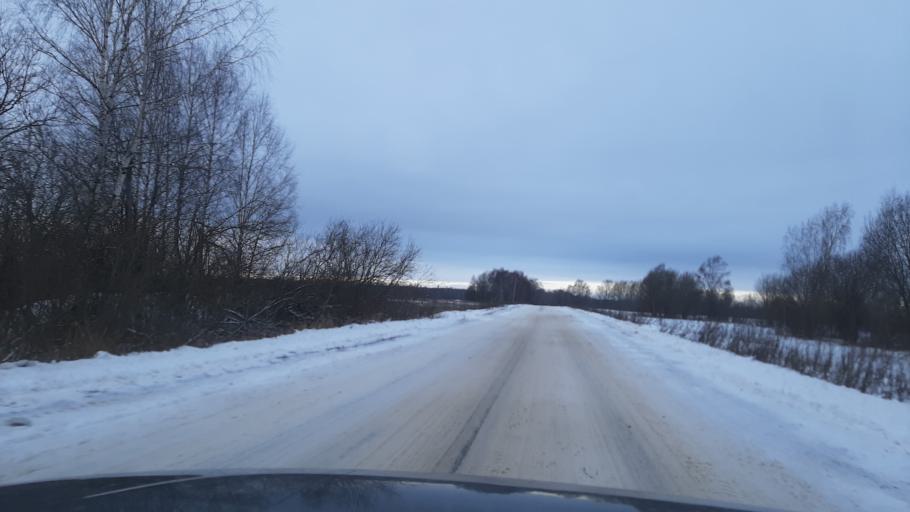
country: RU
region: Kostroma
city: Volgorechensk
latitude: 57.4363
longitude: 41.0570
